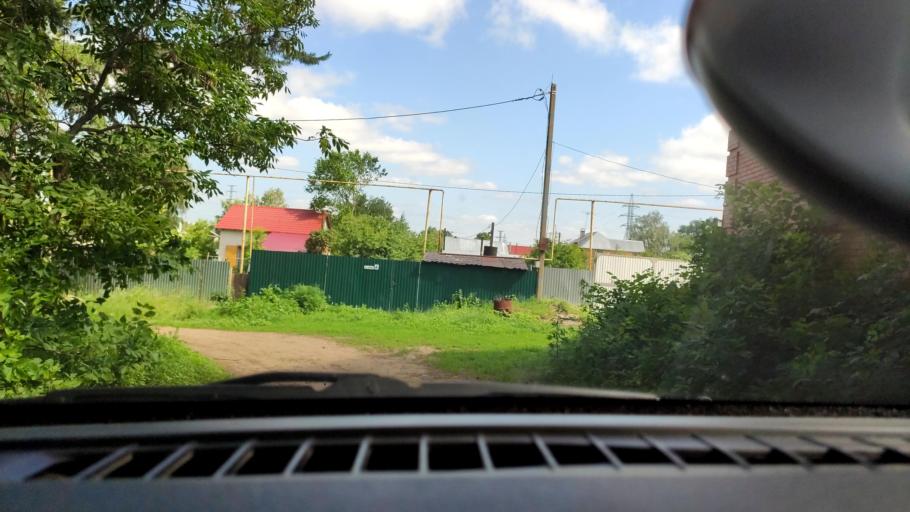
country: RU
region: Samara
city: Samara
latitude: 53.1274
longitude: 50.1853
